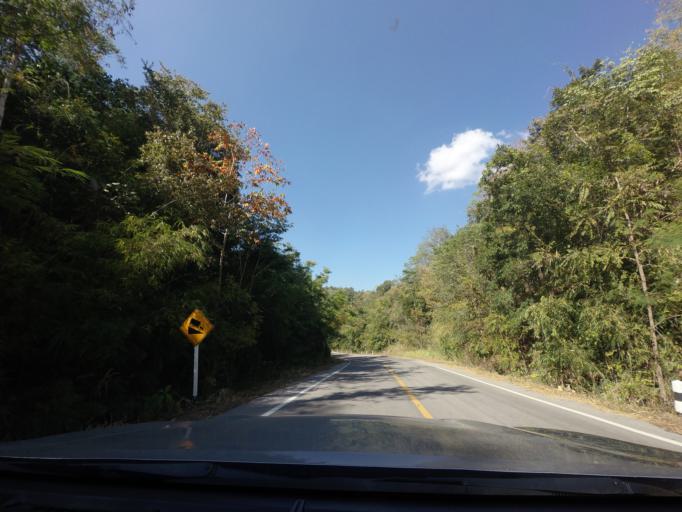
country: TH
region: Lampang
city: Chae Hom
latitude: 18.5490
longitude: 99.6336
